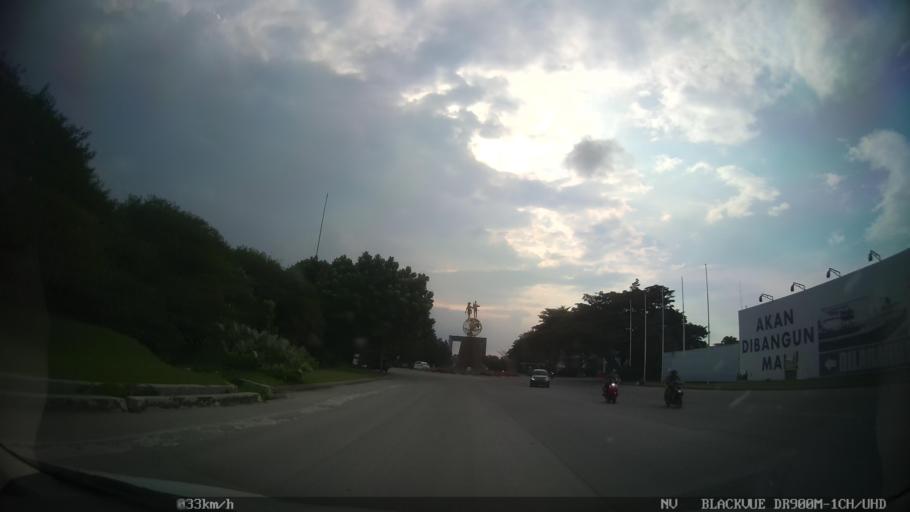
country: ID
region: North Sumatra
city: Medan
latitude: 3.6057
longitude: 98.7272
